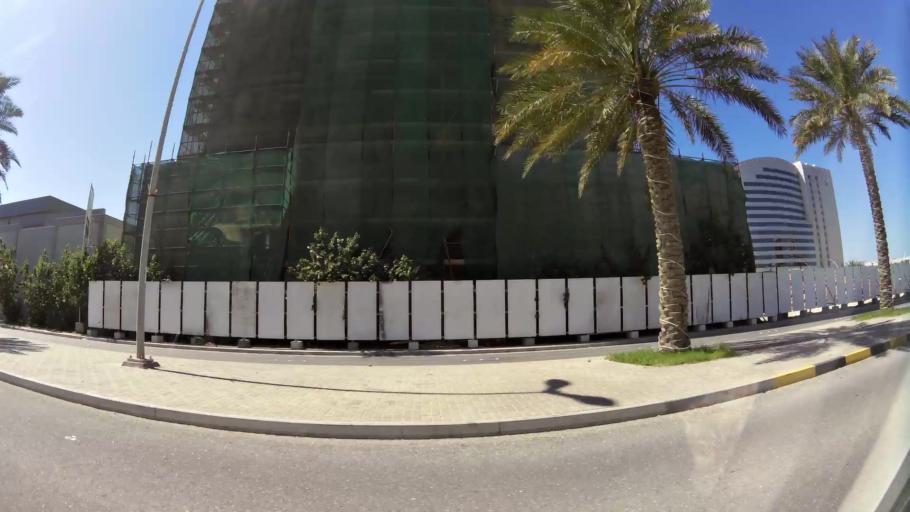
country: BH
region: Muharraq
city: Al Hadd
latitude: 26.2882
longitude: 50.6604
